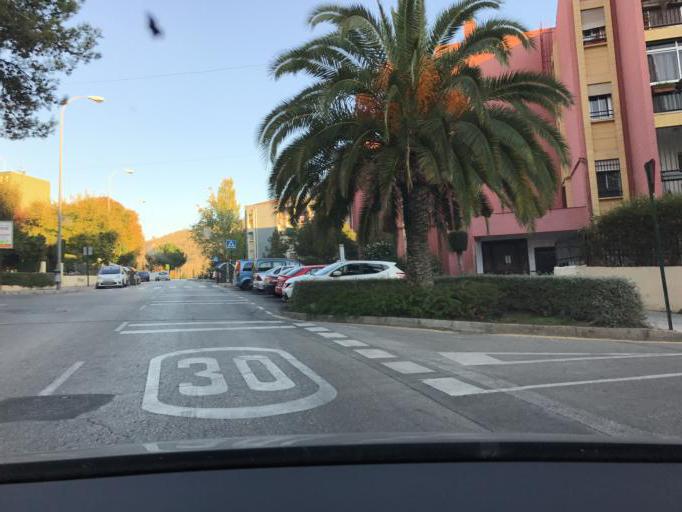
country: ES
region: Andalusia
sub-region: Provincia de Granada
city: Granada
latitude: 37.1975
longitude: -3.6004
